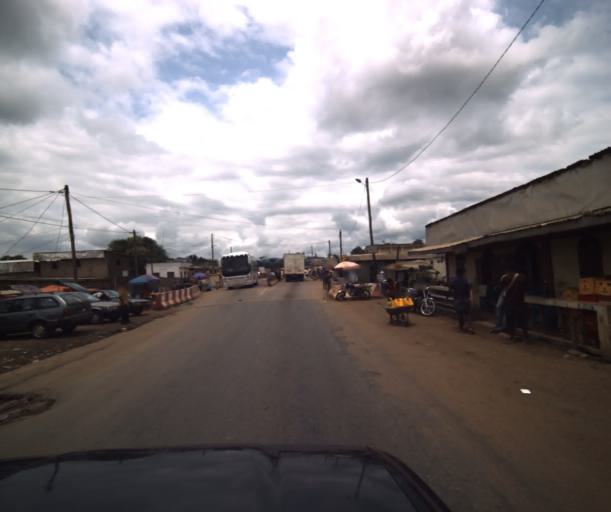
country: CM
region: Centre
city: Eseka
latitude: 3.8830
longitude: 10.8509
